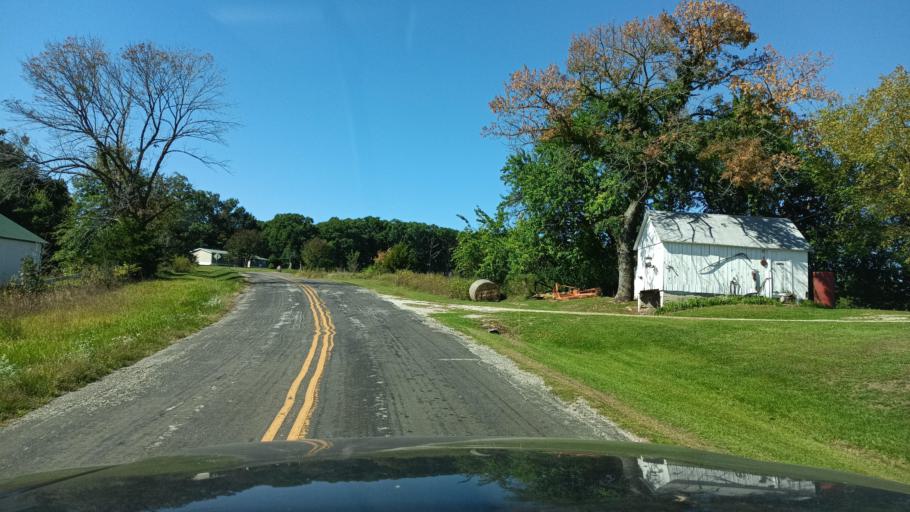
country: US
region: Missouri
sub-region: Scotland County
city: Memphis
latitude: 40.3551
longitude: -92.2544
